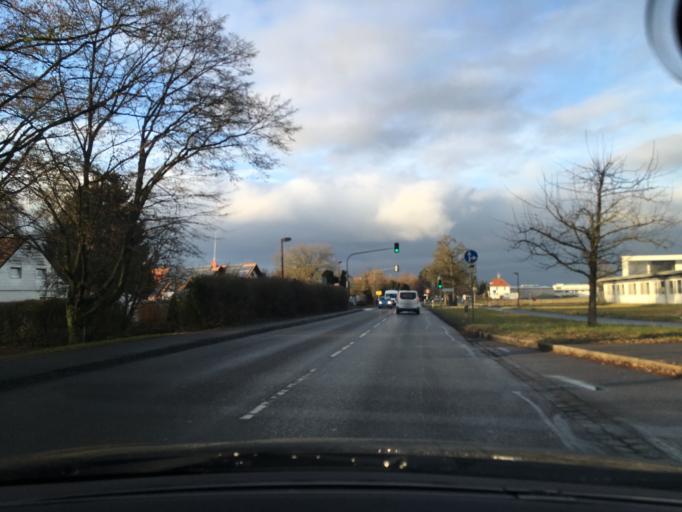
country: DE
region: Baden-Wuerttemberg
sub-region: Tuebingen Region
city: Weingarten
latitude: 47.8192
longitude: 9.6292
